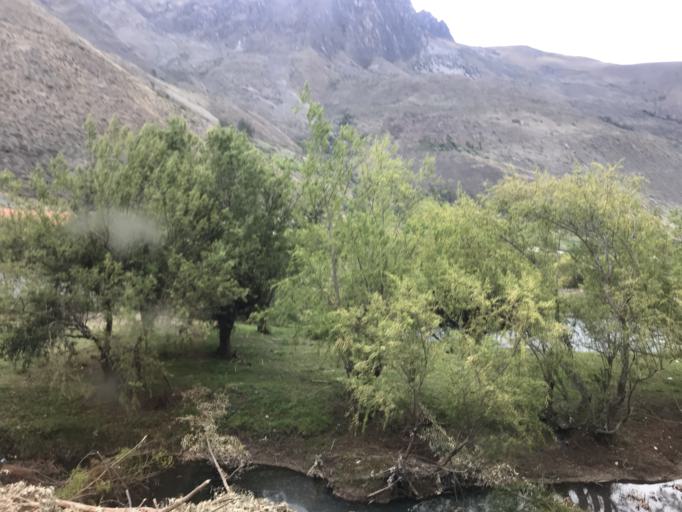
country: PE
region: Cusco
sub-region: Provincia de Urubamba
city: Ollantaytambo
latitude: -13.2534
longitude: -72.2818
